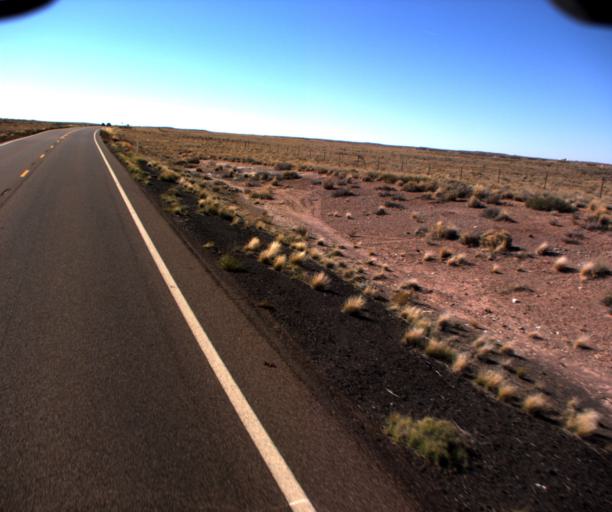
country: US
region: Arizona
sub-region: Navajo County
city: Dilkon
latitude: 35.2391
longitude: -110.4306
